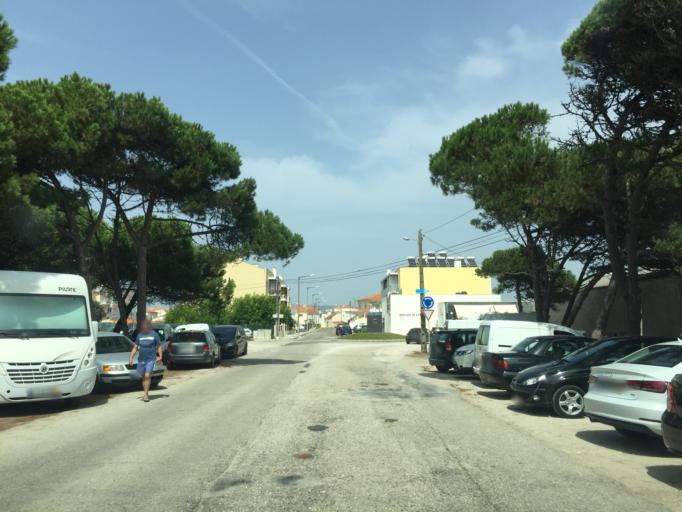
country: PT
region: Coimbra
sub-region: Figueira da Foz
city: Figueira da Foz
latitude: 40.1244
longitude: -8.8576
